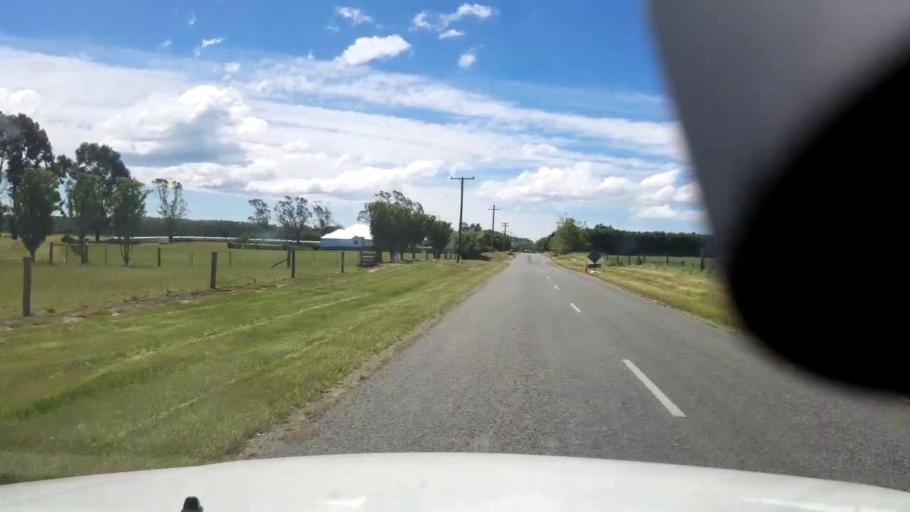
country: NZ
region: Canterbury
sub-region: Timaru District
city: Pleasant Point
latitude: -44.2743
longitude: 171.2533
